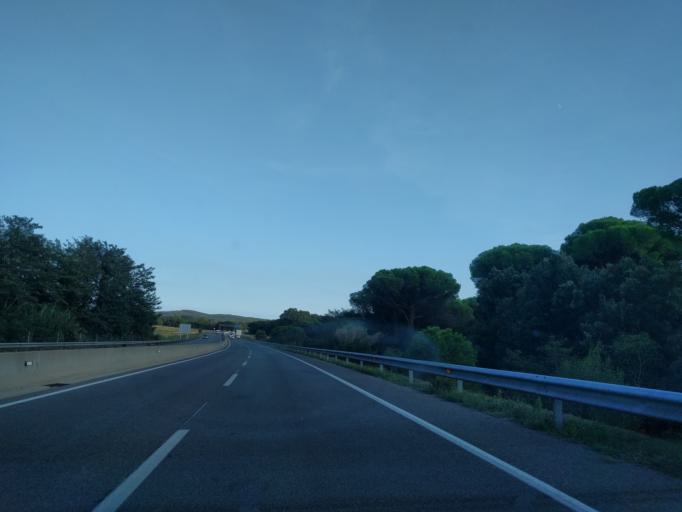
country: ES
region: Catalonia
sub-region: Provincia de Girona
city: Santa Cristina d'Aro
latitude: 41.8173
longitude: 2.9821
